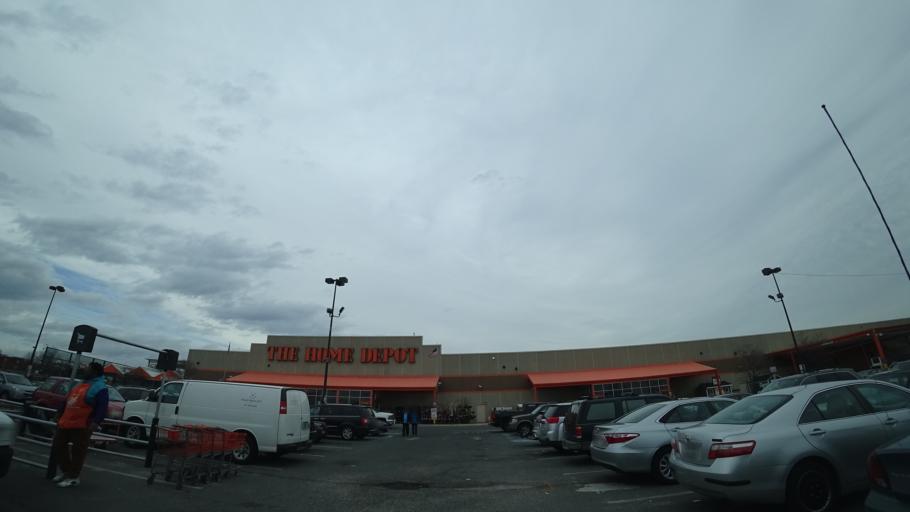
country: US
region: Maryland
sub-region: Prince George's County
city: Mount Rainier
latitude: 38.9203
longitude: -76.9916
